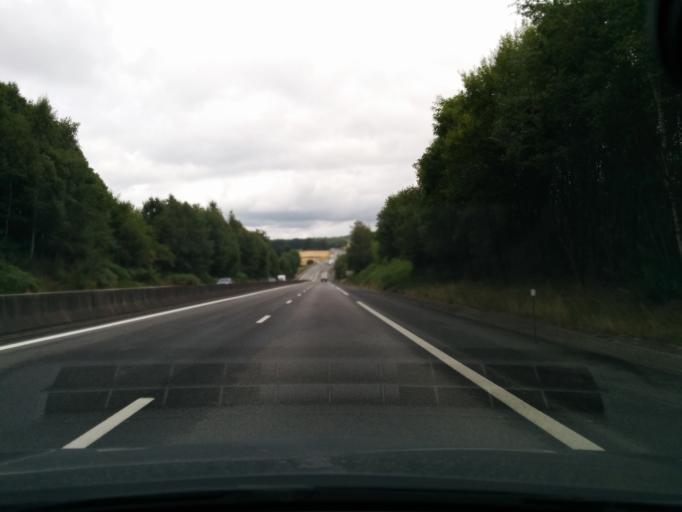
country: FR
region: Limousin
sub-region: Departement de la Correze
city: Uzerche
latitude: 45.3743
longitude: 1.5738
